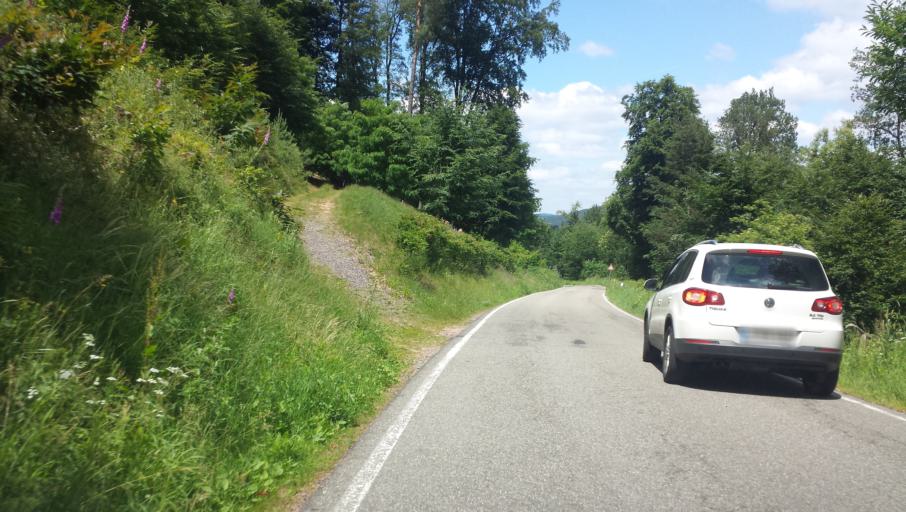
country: DE
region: Rheinland-Pfalz
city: Wernersberg
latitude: 49.1891
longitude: 7.9512
